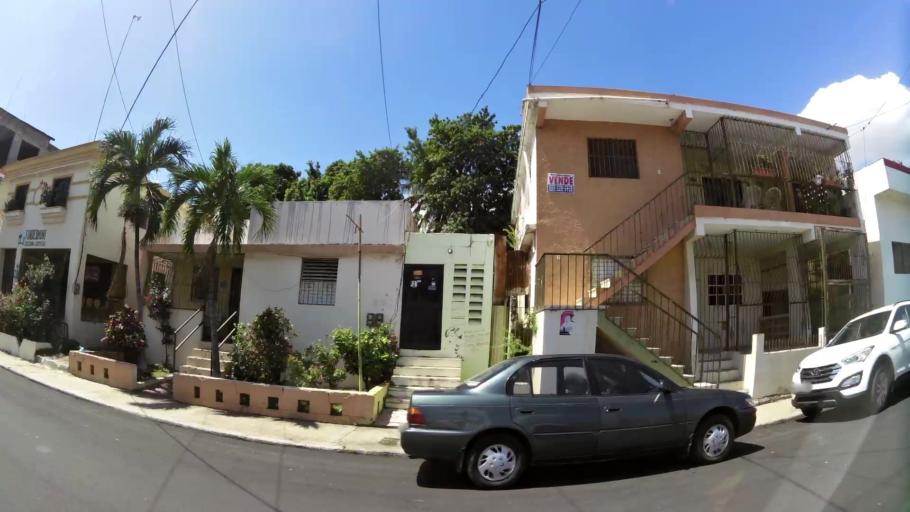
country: DO
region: San Cristobal
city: San Cristobal
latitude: 18.4126
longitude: -70.1072
